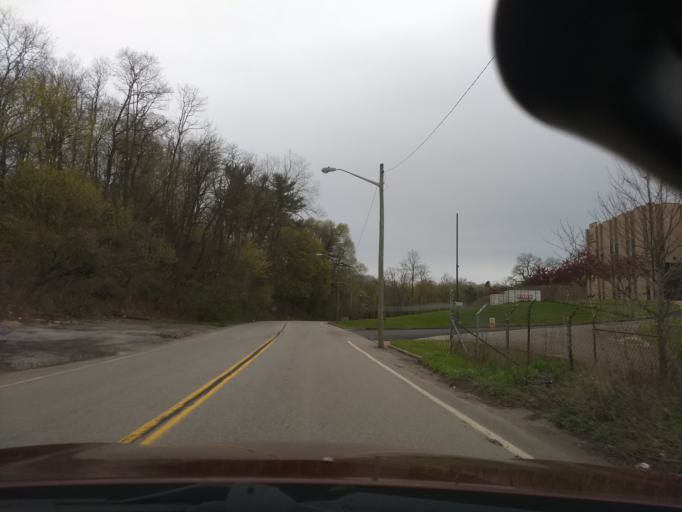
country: US
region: Pennsylvania
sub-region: Allegheny County
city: Mount Oliver
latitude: 40.3931
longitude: -79.9802
